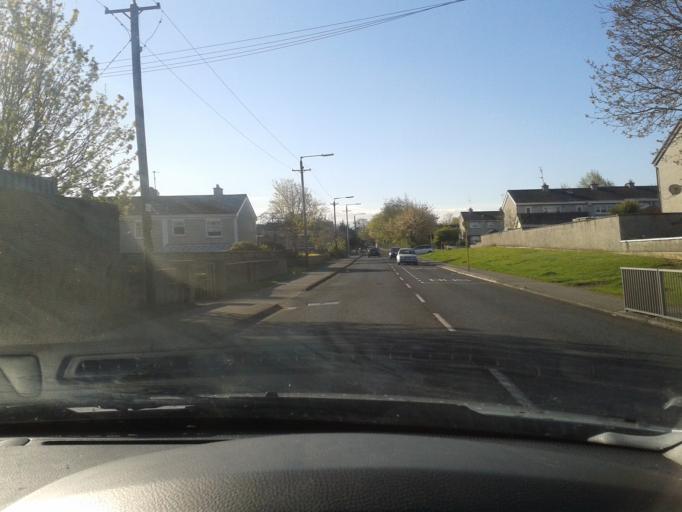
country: IE
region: Leinster
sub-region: Fingal County
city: Swords
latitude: 53.4647
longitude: -6.2353
